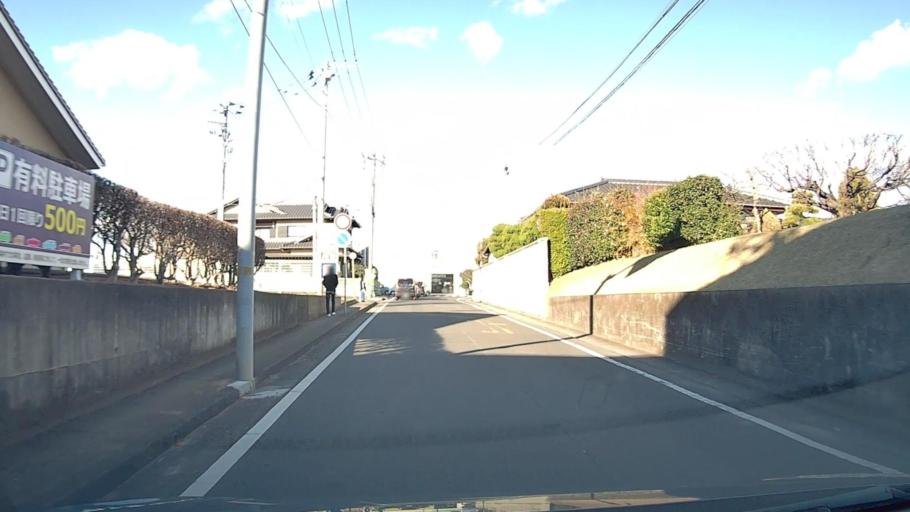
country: JP
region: Ibaraki
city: Mito-shi
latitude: 36.3758
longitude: 140.4450
